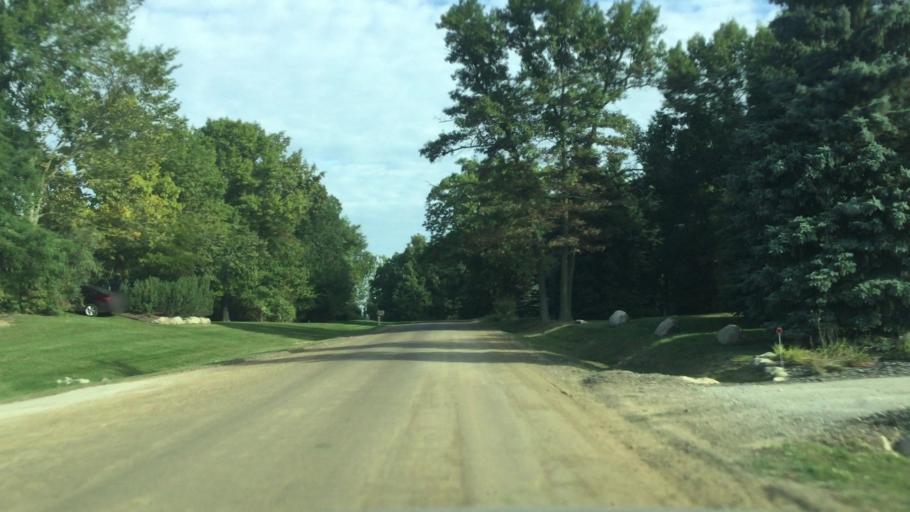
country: US
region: Michigan
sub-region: Livingston County
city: Howell
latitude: 42.6029
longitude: -83.8648
